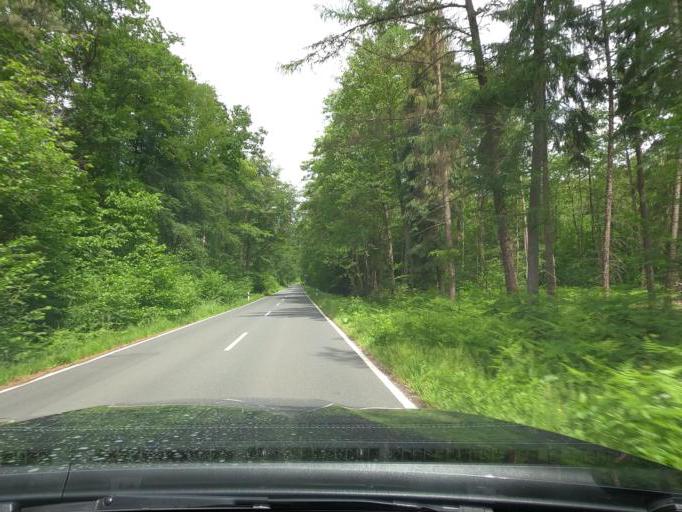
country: DE
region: Lower Saxony
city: Lehrte
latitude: 52.4003
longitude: 9.9274
